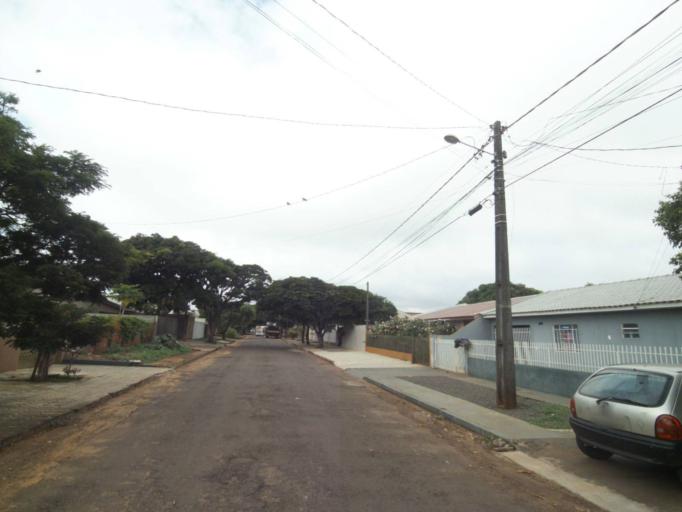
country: BR
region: Parana
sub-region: Campo Mourao
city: Campo Mourao
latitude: -24.0245
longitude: -52.3624
